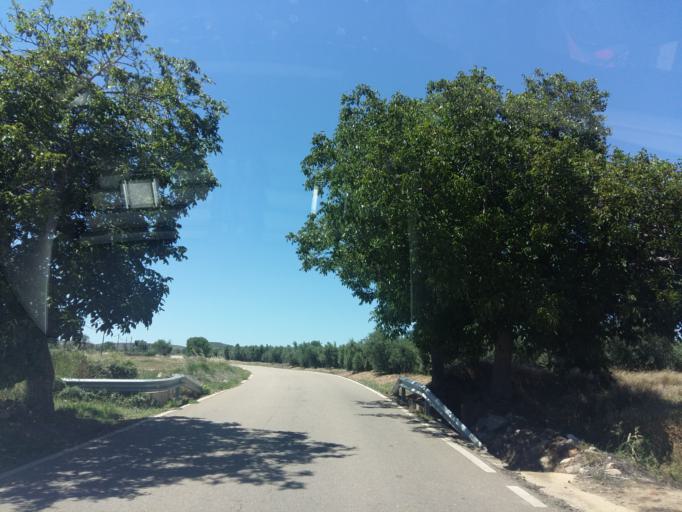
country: ES
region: Aragon
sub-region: Provincia de Zaragoza
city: Vera de Moncayo
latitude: 41.8266
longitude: -1.6933
